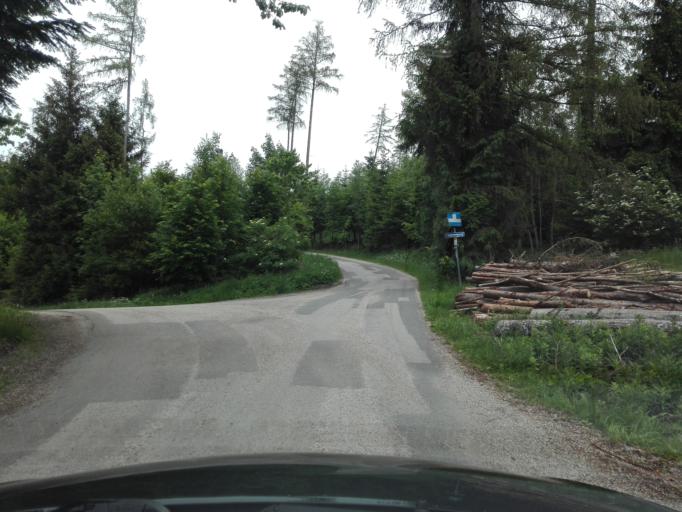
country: AT
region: Upper Austria
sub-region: Politischer Bezirk Gmunden
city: Scharnstein
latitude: 47.9374
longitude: 13.9562
